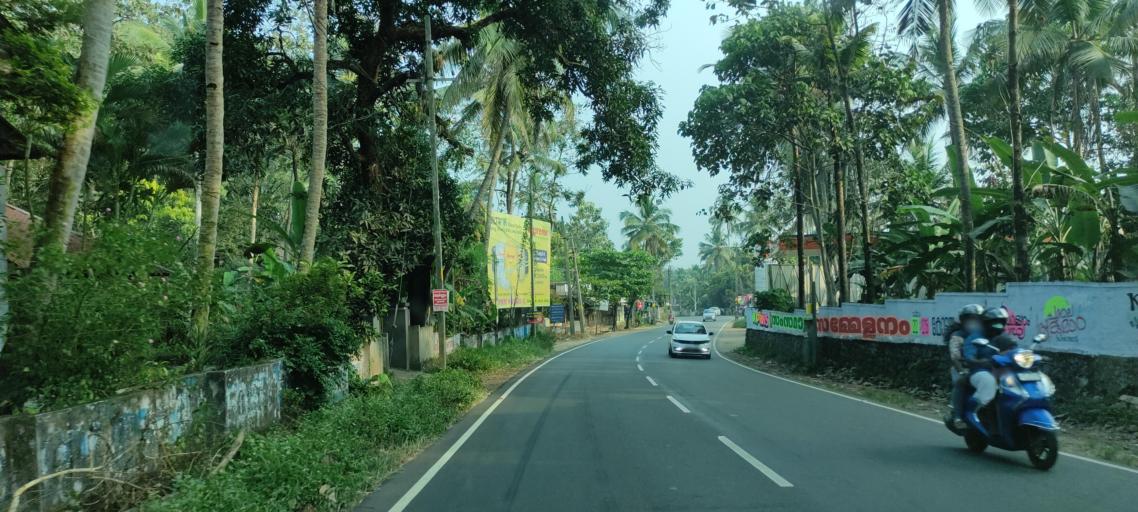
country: IN
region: Kerala
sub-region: Kottayam
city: Vaikam
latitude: 9.7580
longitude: 76.4960
